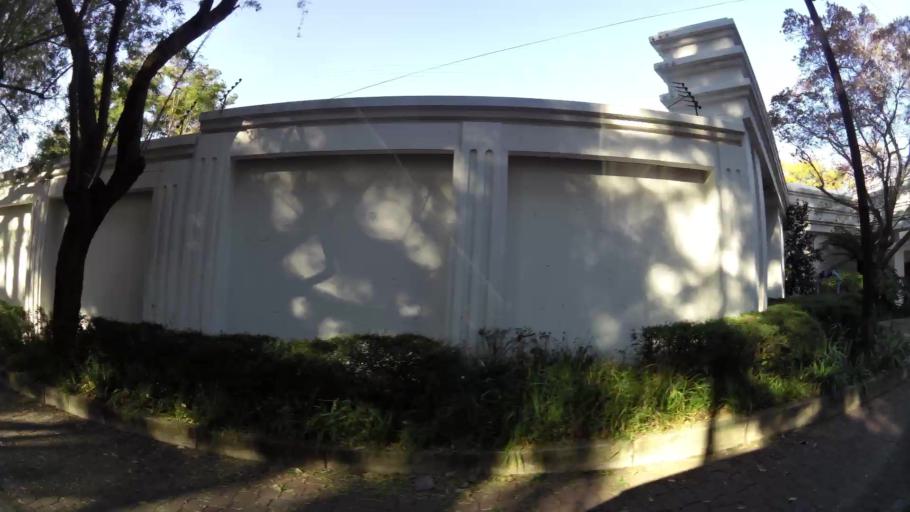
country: ZA
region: Gauteng
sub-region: City of Johannesburg Metropolitan Municipality
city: Johannesburg
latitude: -26.1095
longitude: 28.0661
